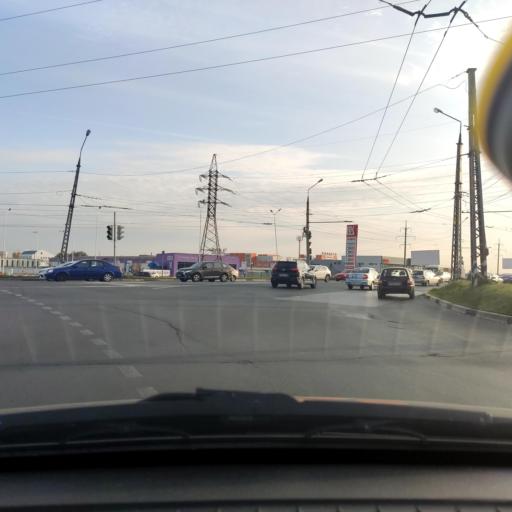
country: RU
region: Samara
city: Tol'yatti
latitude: 53.5510
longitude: 49.3183
